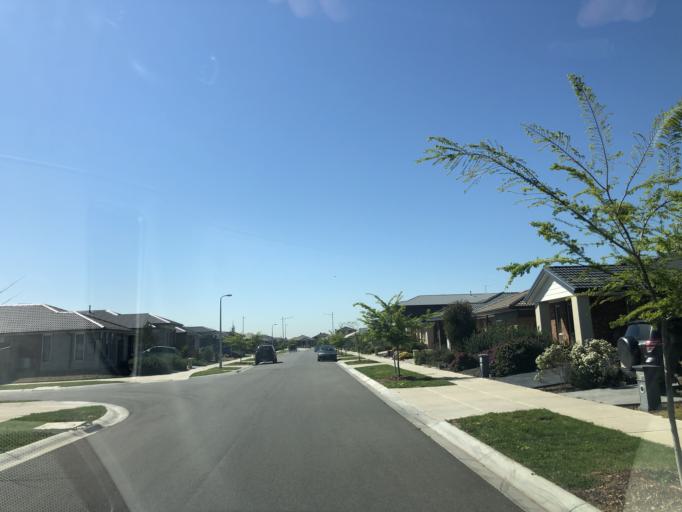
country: AU
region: Victoria
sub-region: Wyndham
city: Point Cook
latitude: -37.9067
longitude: 144.7226
